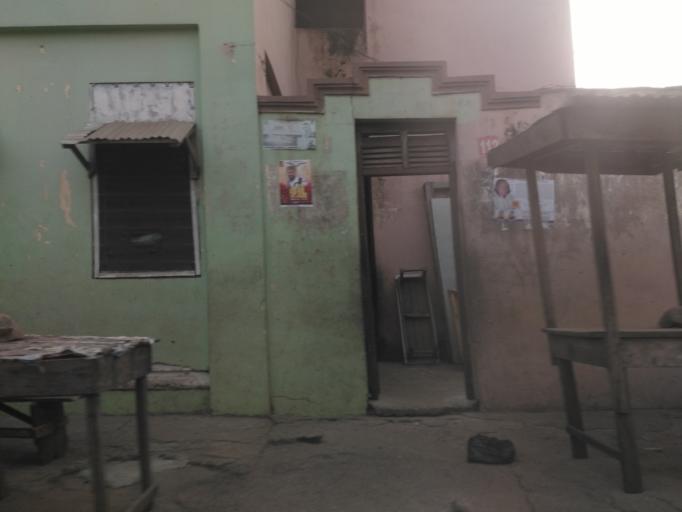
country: GH
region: Ashanti
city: Kumasi
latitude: 6.7052
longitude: -1.6190
